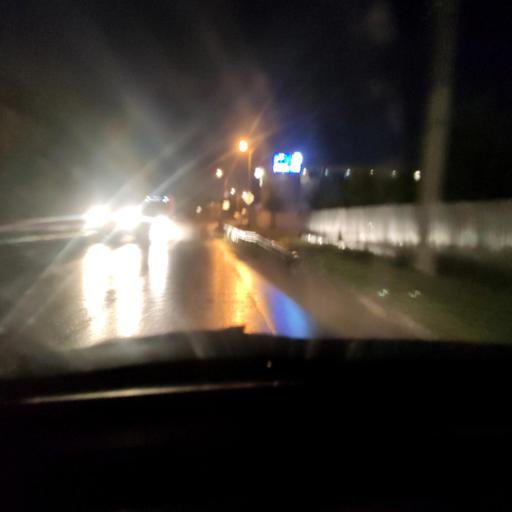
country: RU
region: Samara
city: Syzran'
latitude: 53.1661
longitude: 48.4933
